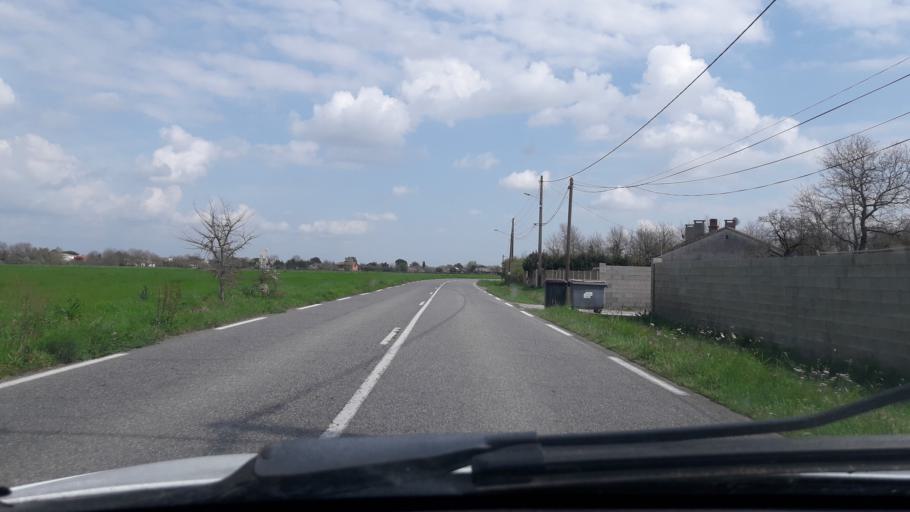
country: FR
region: Midi-Pyrenees
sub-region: Departement de la Haute-Garonne
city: Seysses
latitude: 43.5011
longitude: 1.2808
